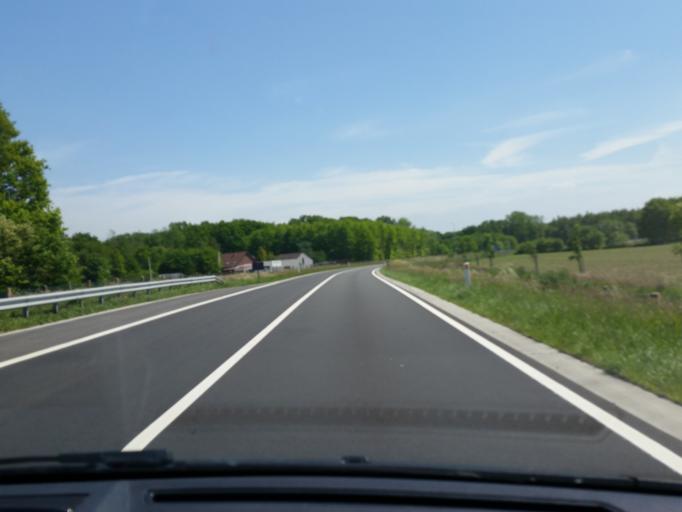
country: BE
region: Flanders
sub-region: Provincie Antwerpen
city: Bonheiden
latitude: 51.0407
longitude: 4.5606
